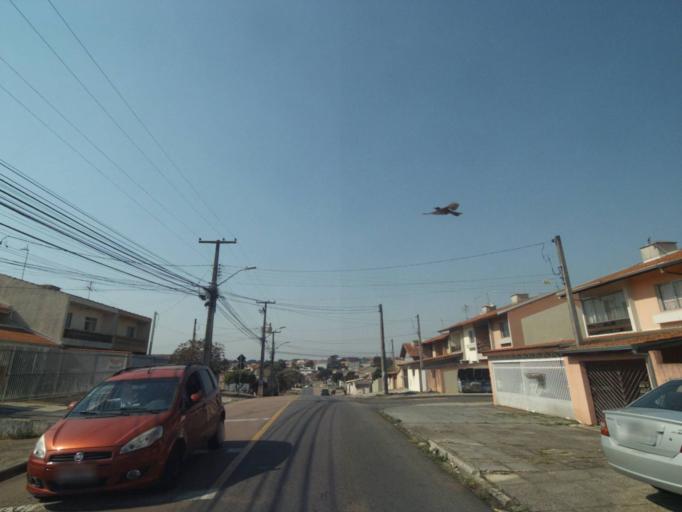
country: BR
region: Parana
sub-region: Sao Jose Dos Pinhais
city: Sao Jose dos Pinhais
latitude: -25.4962
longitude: -49.2629
